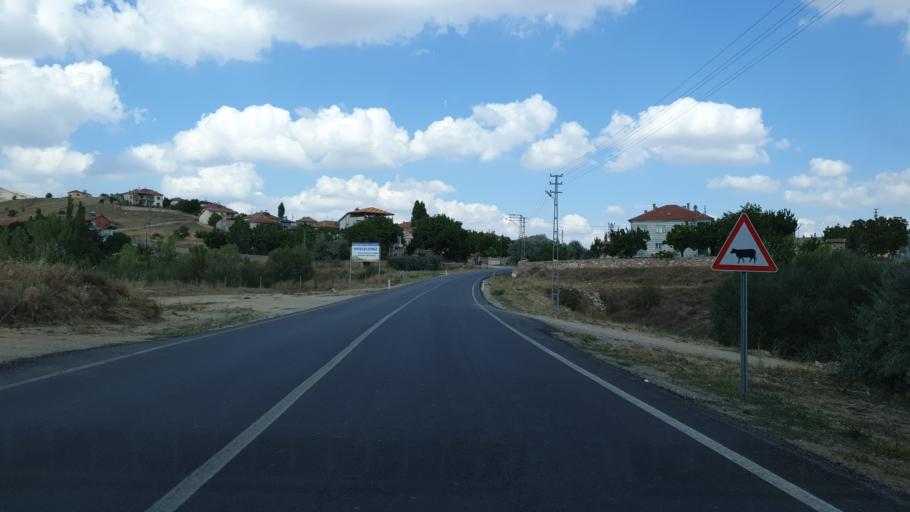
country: TR
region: Kayseri
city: Felahiye
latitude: 39.1075
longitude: 35.5997
